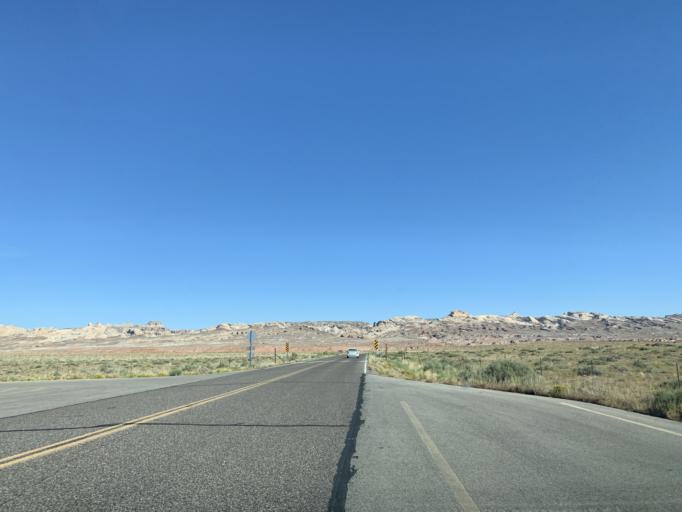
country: US
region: Utah
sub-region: Emery County
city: Ferron
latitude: 38.5784
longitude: -110.7077
